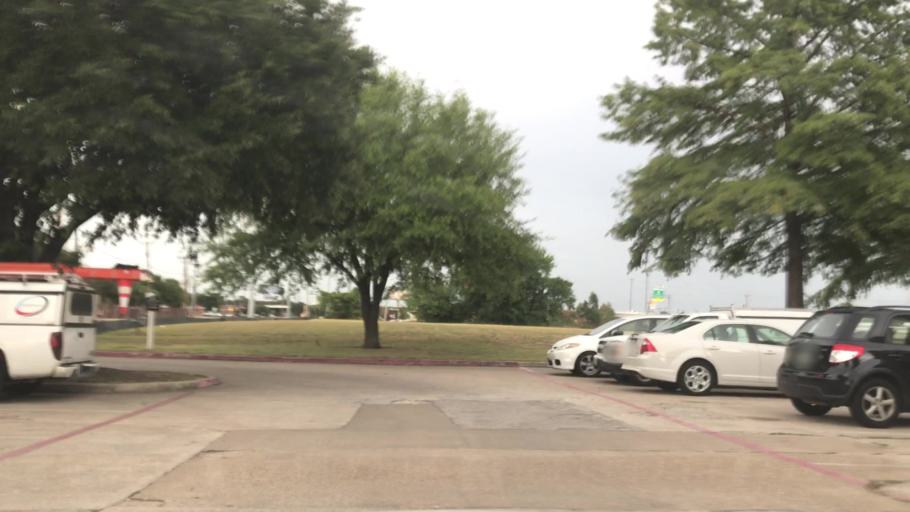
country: US
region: Texas
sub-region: Dallas County
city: Rowlett
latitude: 32.8509
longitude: -96.5742
